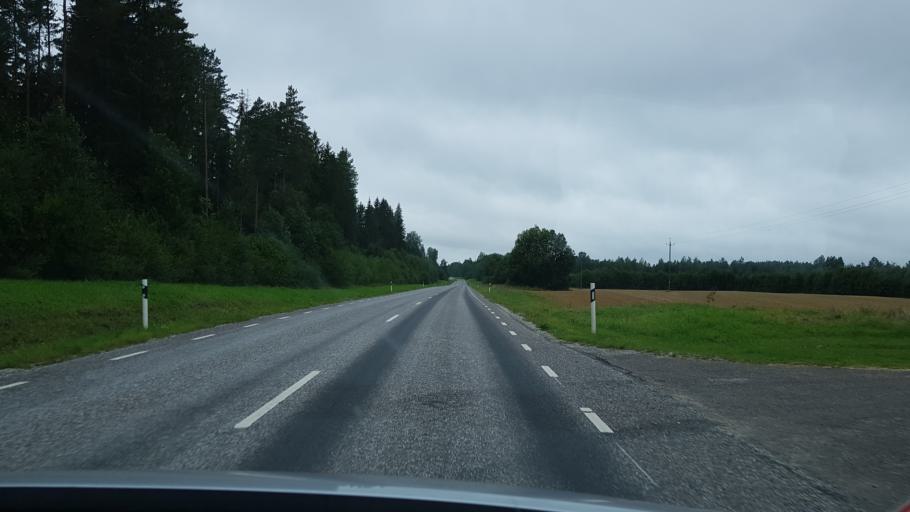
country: EE
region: Vorumaa
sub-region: Antsla vald
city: Vana-Antsla
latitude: 58.0005
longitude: 26.7138
